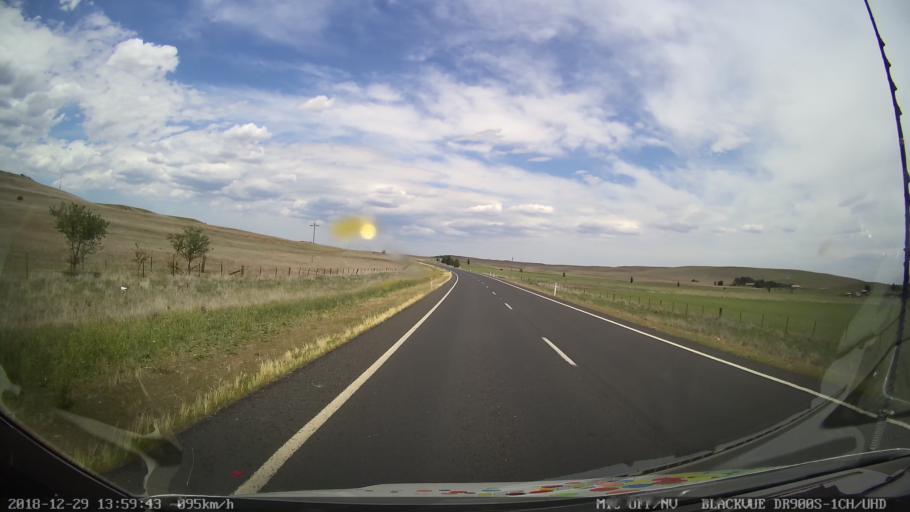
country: AU
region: New South Wales
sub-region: Cooma-Monaro
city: Cooma
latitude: -36.2563
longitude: 149.1506
